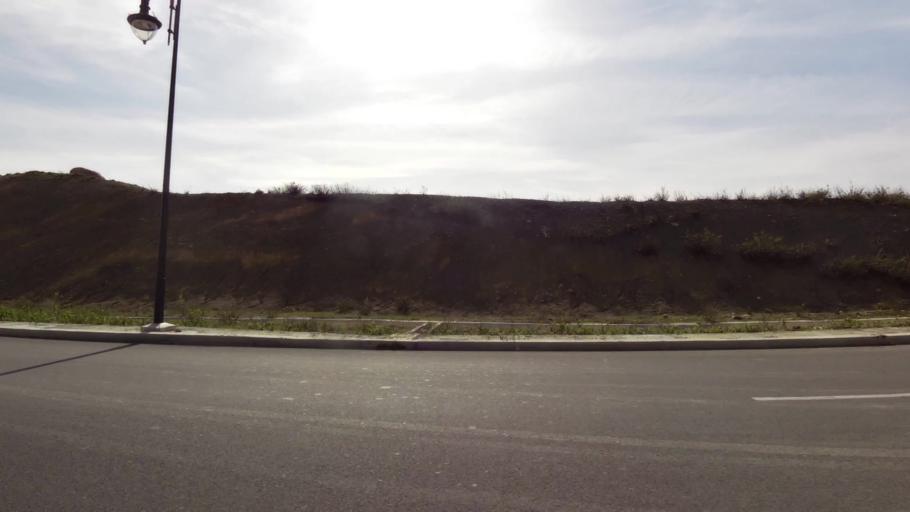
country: MA
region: Tanger-Tetouan
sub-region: Tanger-Assilah
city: Tangier
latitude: 35.7047
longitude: -5.7935
